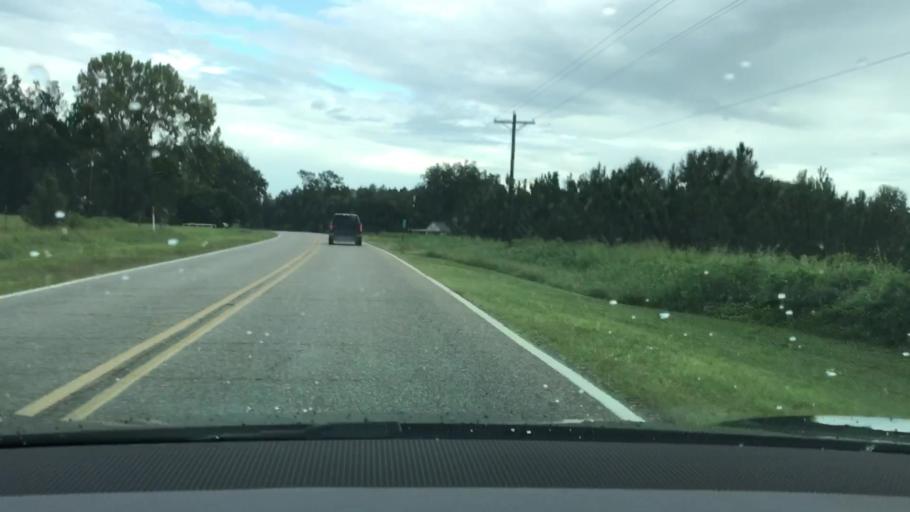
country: US
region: Alabama
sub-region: Geneva County
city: Samson
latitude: 31.1302
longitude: -86.1321
